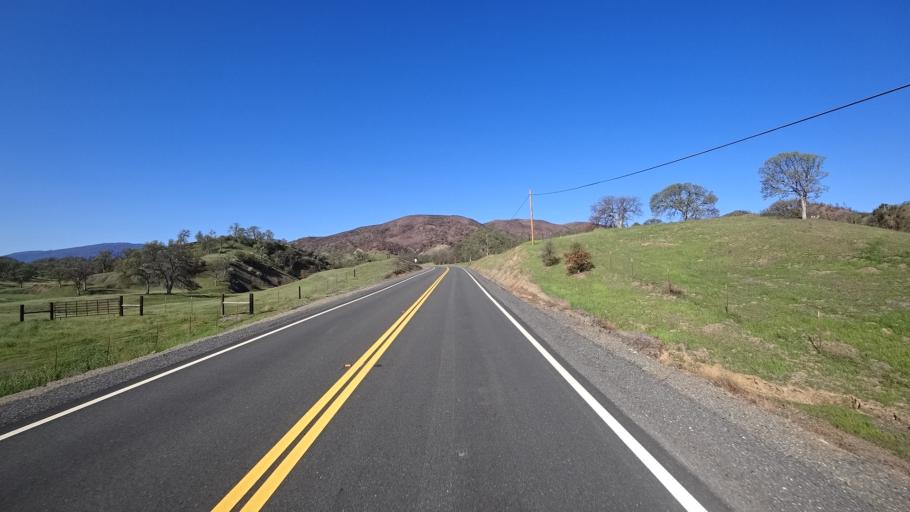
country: US
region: California
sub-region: Glenn County
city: Orland
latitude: 39.6548
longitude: -122.5826
